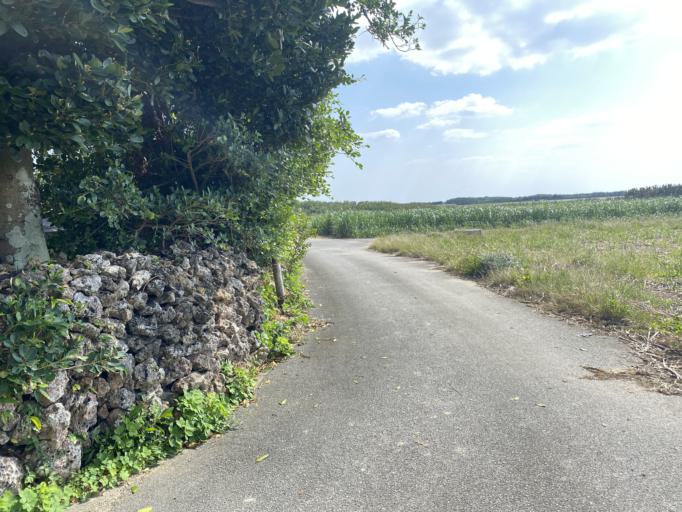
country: JP
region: Okinawa
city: Ishigaki
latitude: 24.0603
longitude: 123.7745
